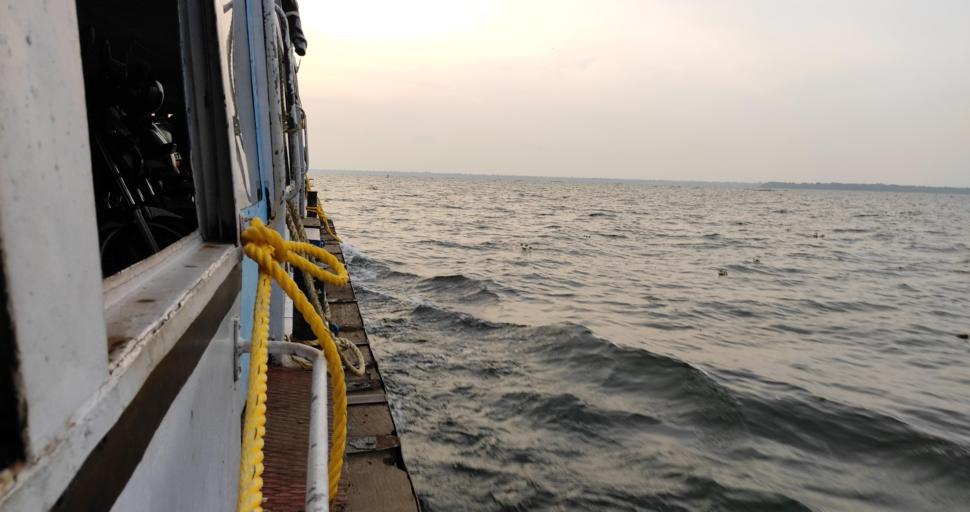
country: IN
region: Kerala
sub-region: Alappuzha
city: Shertallai
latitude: 9.6019
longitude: 76.4009
